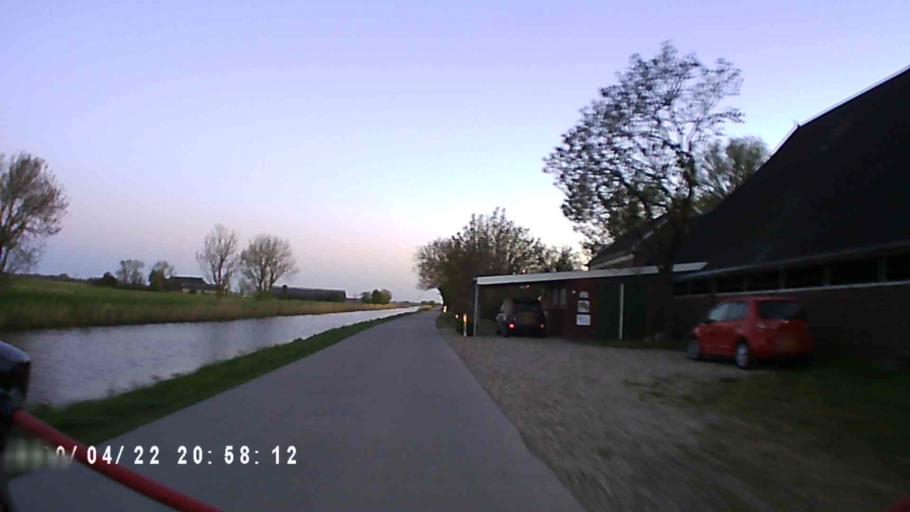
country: NL
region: Groningen
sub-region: Gemeente Winsum
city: Winsum
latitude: 53.3256
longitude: 6.5647
